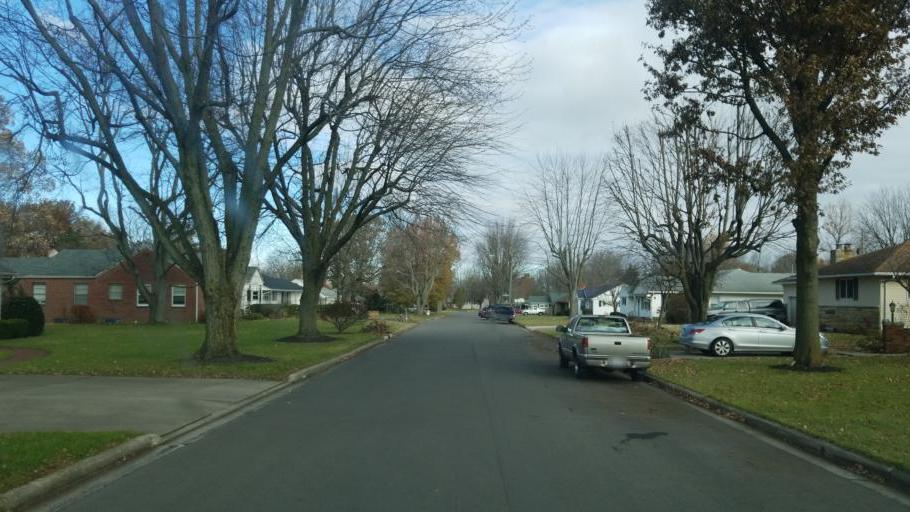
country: US
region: Ohio
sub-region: Hardin County
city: Kenton
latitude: 40.6557
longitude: -83.6040
